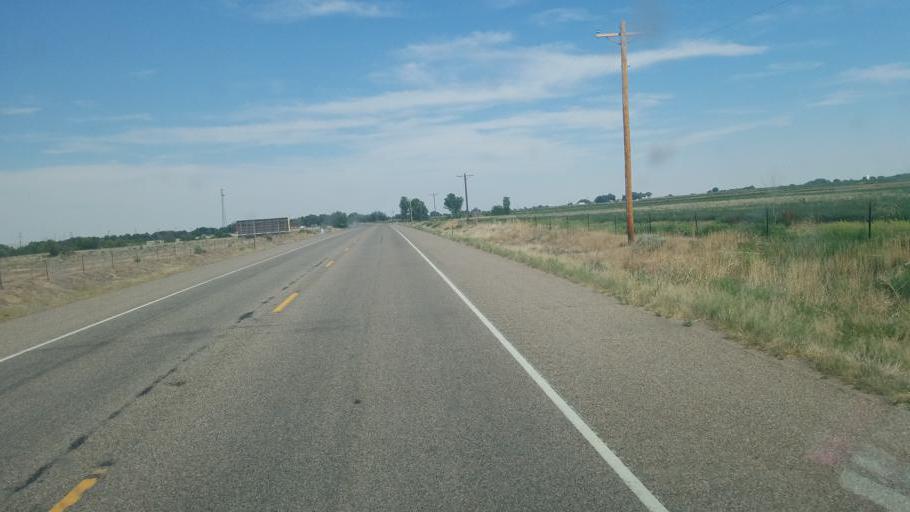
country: US
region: Colorado
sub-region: Pueblo County
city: Pueblo
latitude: 38.2319
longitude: -104.3148
